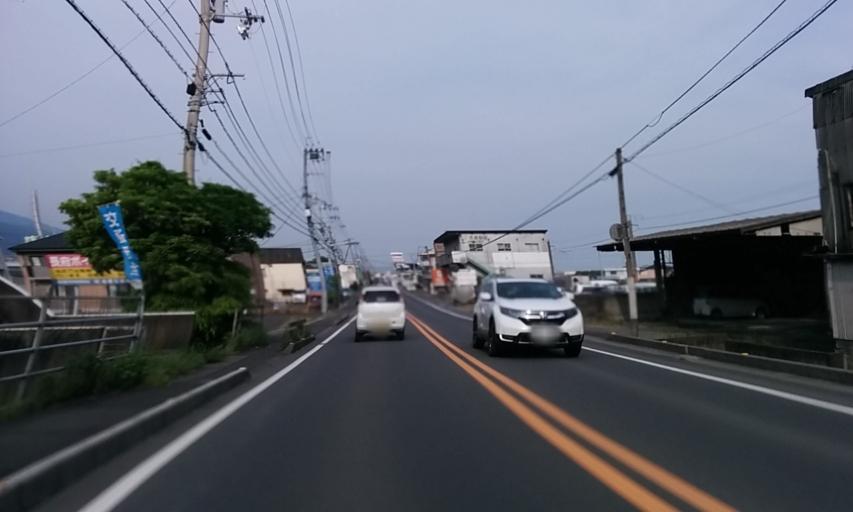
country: JP
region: Ehime
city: Kawanoecho
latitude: 33.9681
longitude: 133.5144
